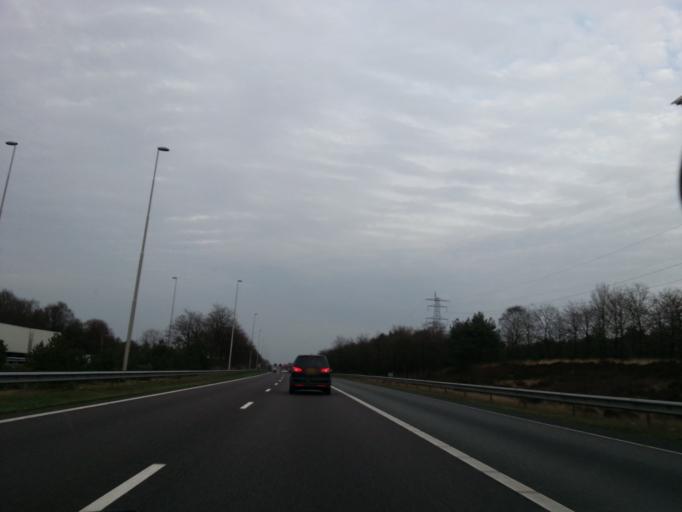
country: NL
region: Gelderland
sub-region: Gemeente Rozendaal
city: Rozendaal
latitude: 52.0411
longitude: 5.9331
